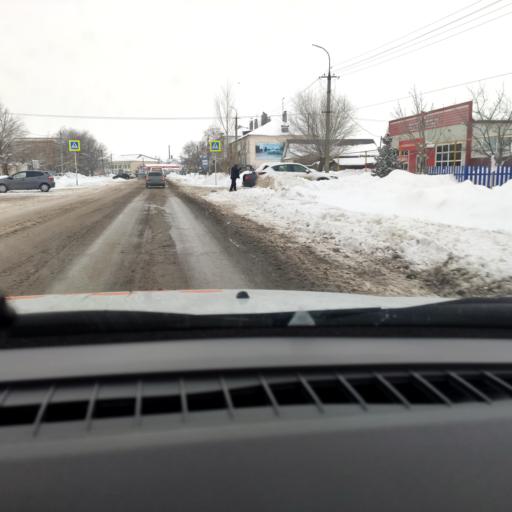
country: RU
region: Saratov
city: Perelyub
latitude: 52.0979
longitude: 50.8664
